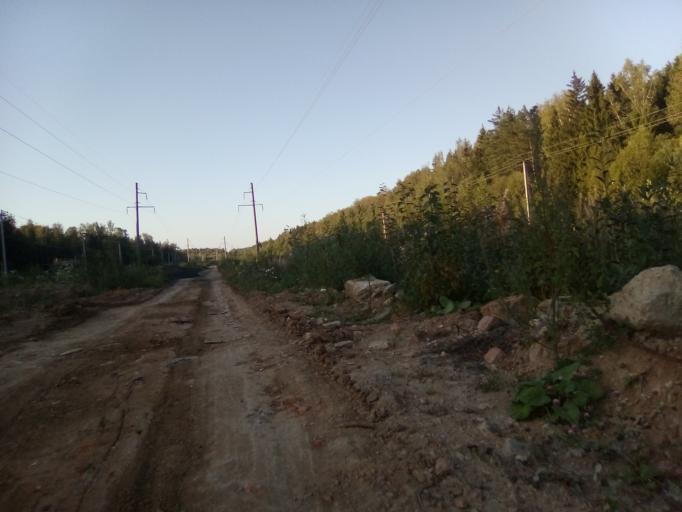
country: RU
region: Moskovskaya
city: Aprelevka
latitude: 55.5717
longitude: 37.0658
